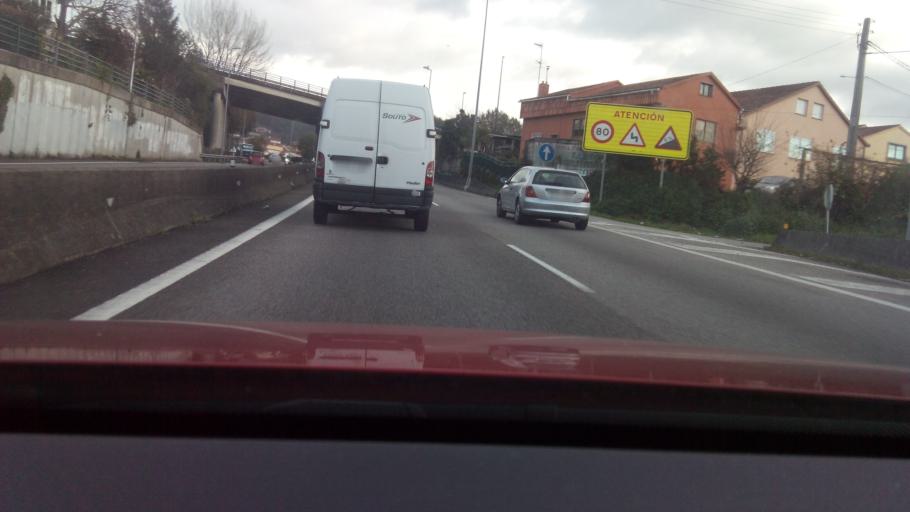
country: ES
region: Galicia
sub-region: Provincia de Pontevedra
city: Vigo
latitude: 42.2084
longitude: -8.6973
